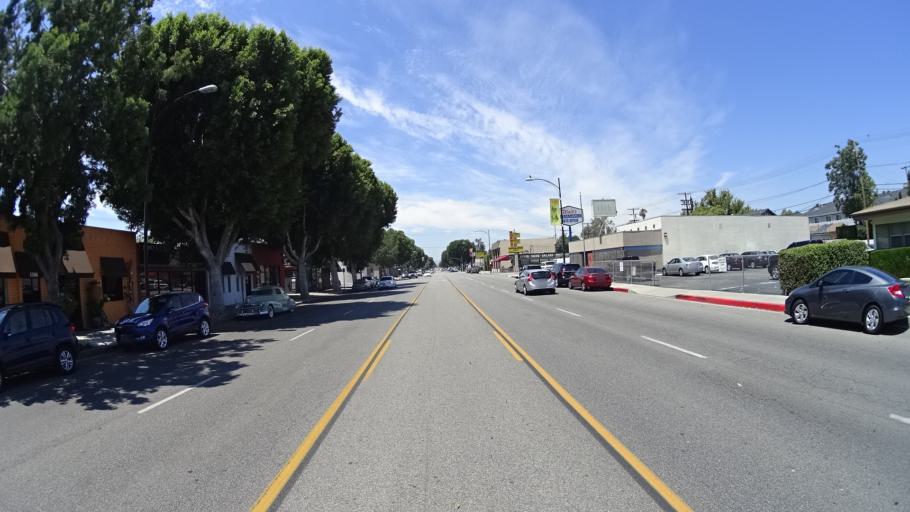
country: US
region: California
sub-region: Los Angeles County
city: Burbank
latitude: 34.1767
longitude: -118.3207
